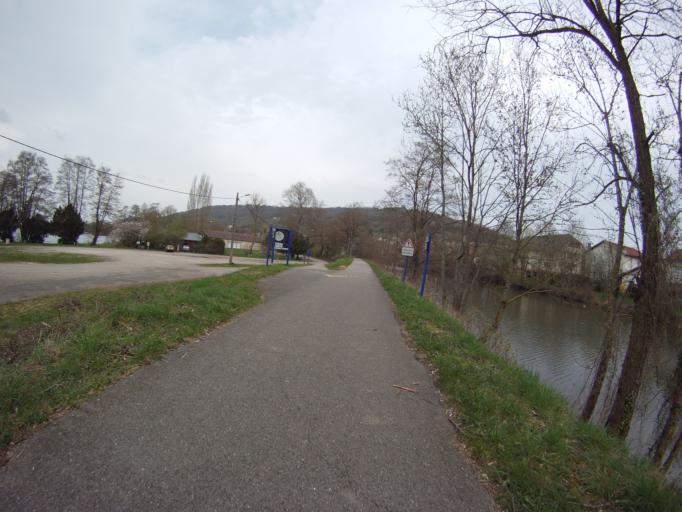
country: FR
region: Lorraine
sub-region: Departement de Meurthe-et-Moselle
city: Messein
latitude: 48.6075
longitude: 6.1493
